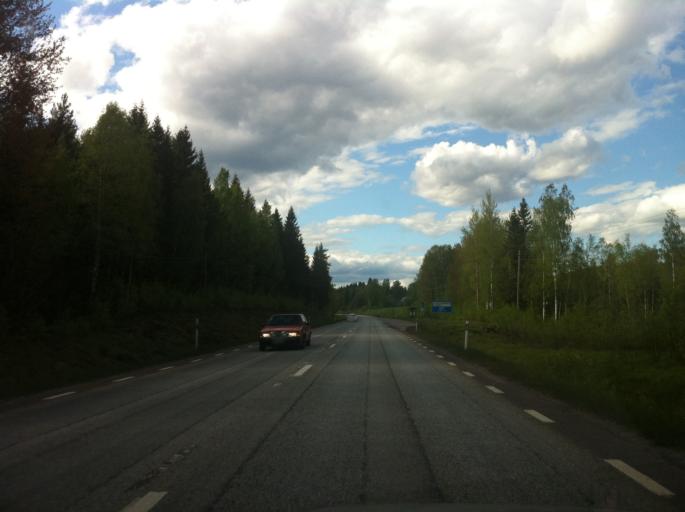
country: SE
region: Vaermland
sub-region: Filipstads Kommun
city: Filipstad
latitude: 59.6821
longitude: 14.2033
